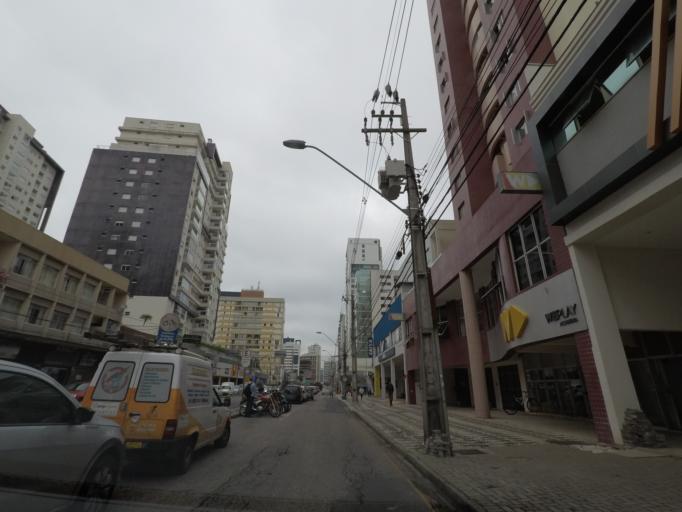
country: BR
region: Parana
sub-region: Curitiba
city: Curitiba
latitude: -25.4557
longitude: -49.2884
